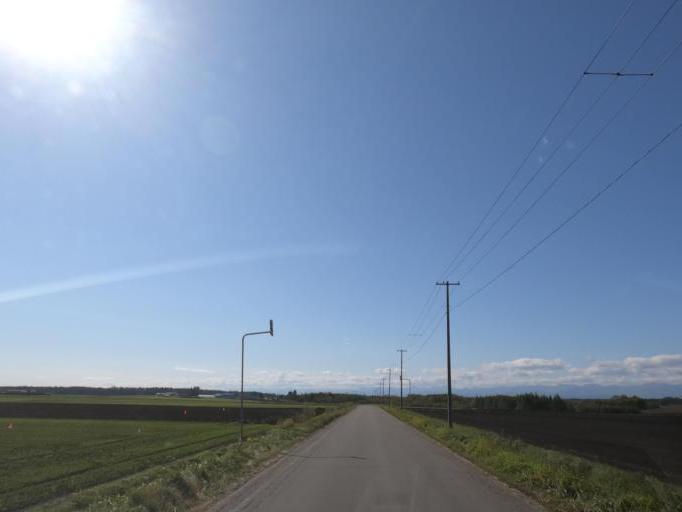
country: JP
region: Hokkaido
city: Obihiro
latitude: 42.8047
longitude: 143.2611
